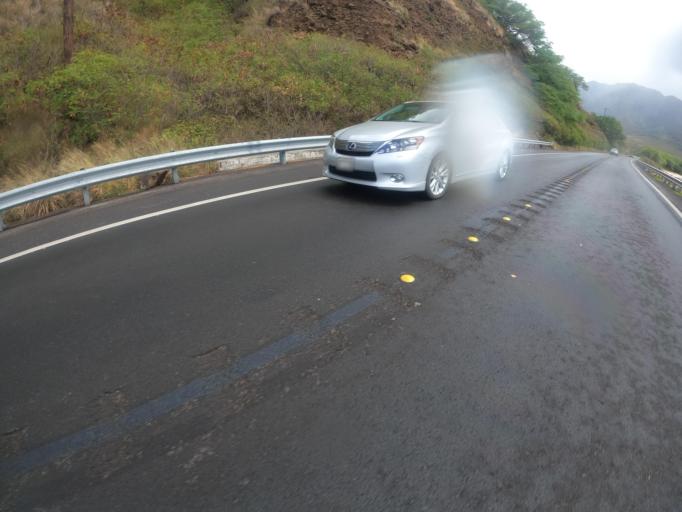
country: US
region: Hawaii
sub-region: Honolulu County
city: Makaha Valley
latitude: 21.5395
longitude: -158.2333
